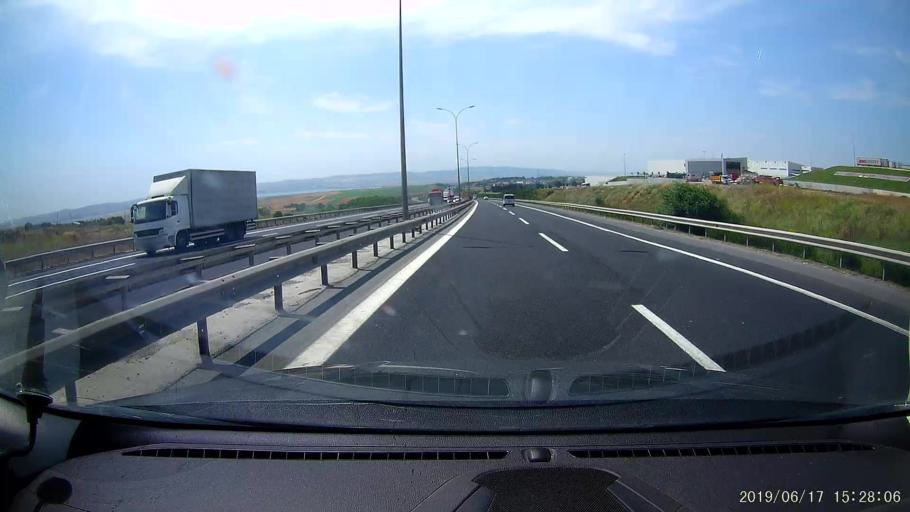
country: TR
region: Istanbul
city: Bueyuekcekmece
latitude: 41.1002
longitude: 28.6112
